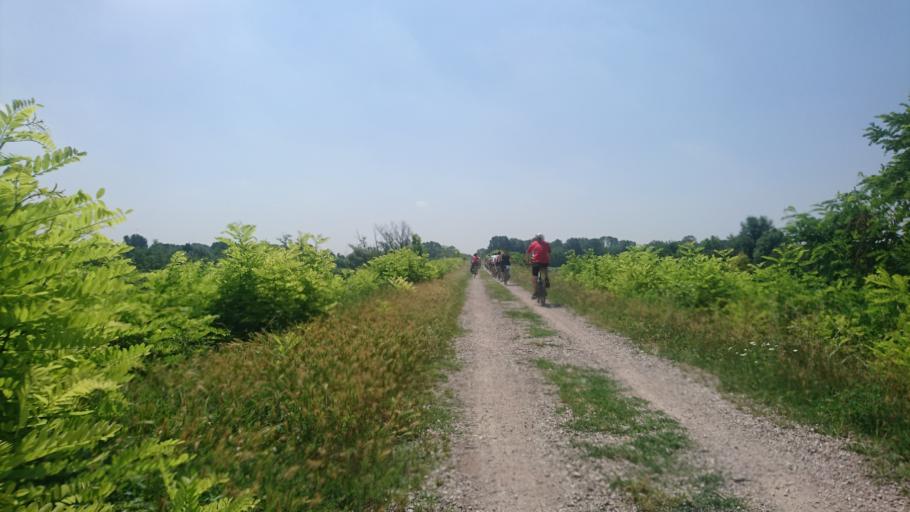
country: IT
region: Veneto
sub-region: Provincia di Venezia
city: Vigonovo
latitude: 45.3998
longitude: 12.0038
